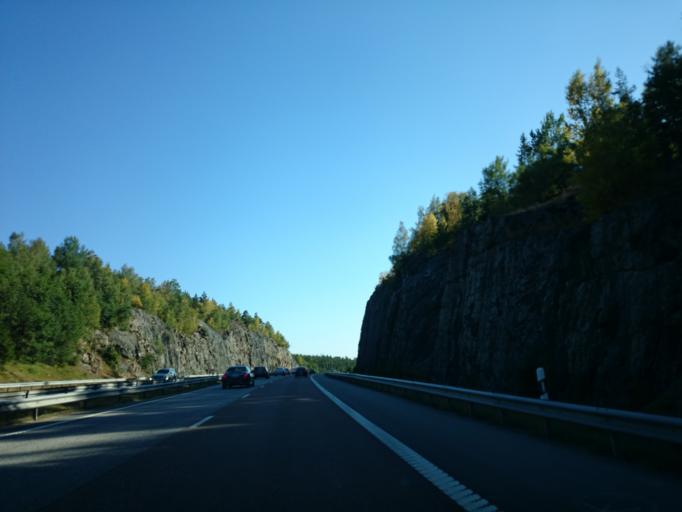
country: SE
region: Stockholm
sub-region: Sodertalje Kommun
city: Pershagen
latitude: 59.1353
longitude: 17.6458
